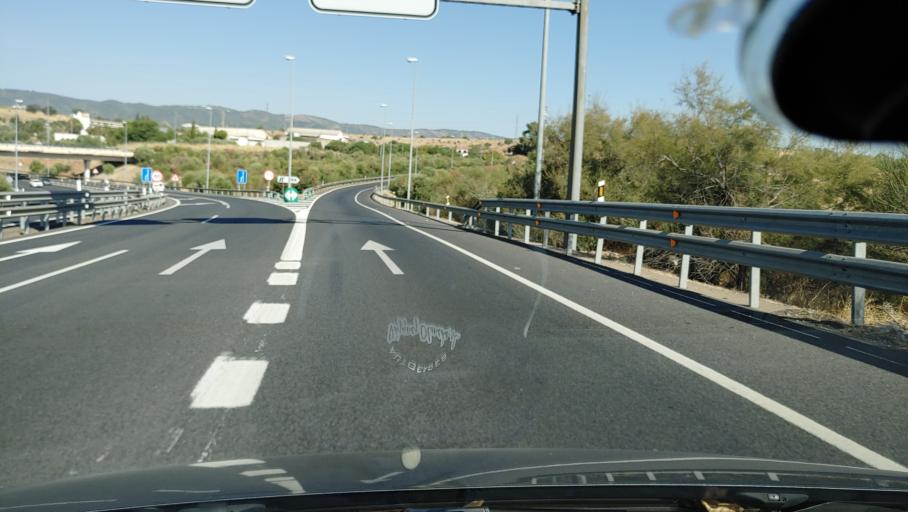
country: ES
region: Andalusia
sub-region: Province of Cordoba
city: Cordoba
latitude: 37.9056
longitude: -4.7520
